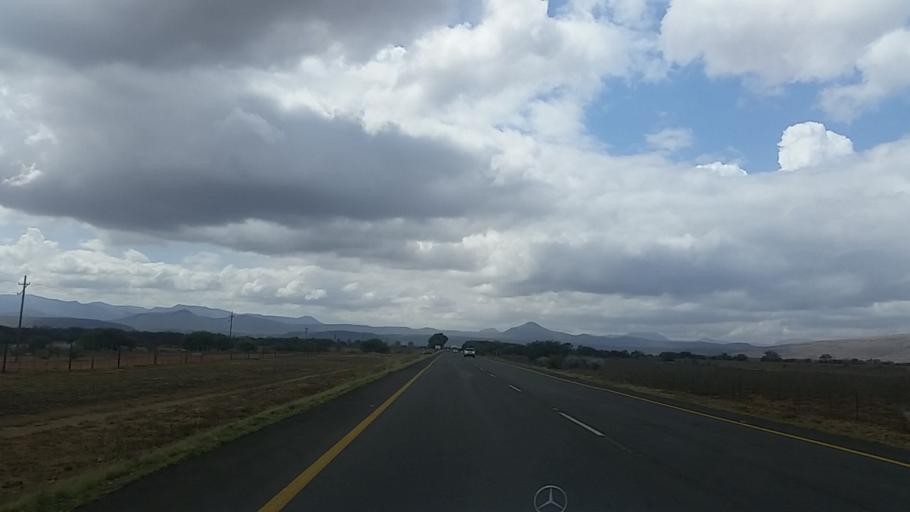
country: ZA
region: Eastern Cape
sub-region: Cacadu District Municipality
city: Graaff-Reinet
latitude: -32.2150
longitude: 24.5448
